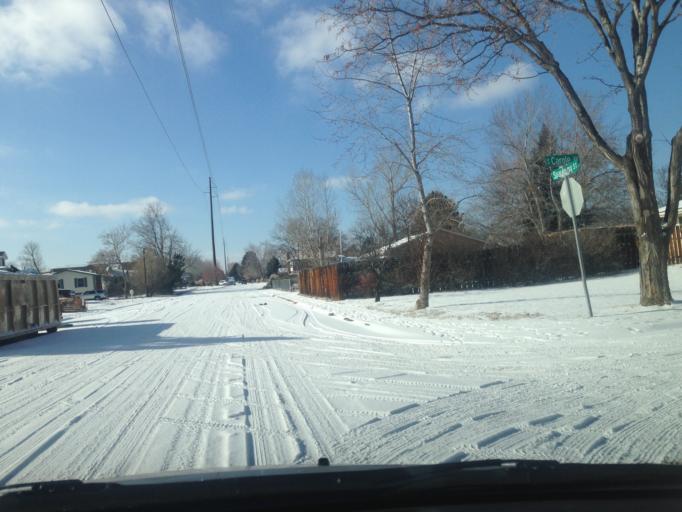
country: US
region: Colorado
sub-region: Boulder County
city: Lafayette
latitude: 39.9906
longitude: -105.0935
